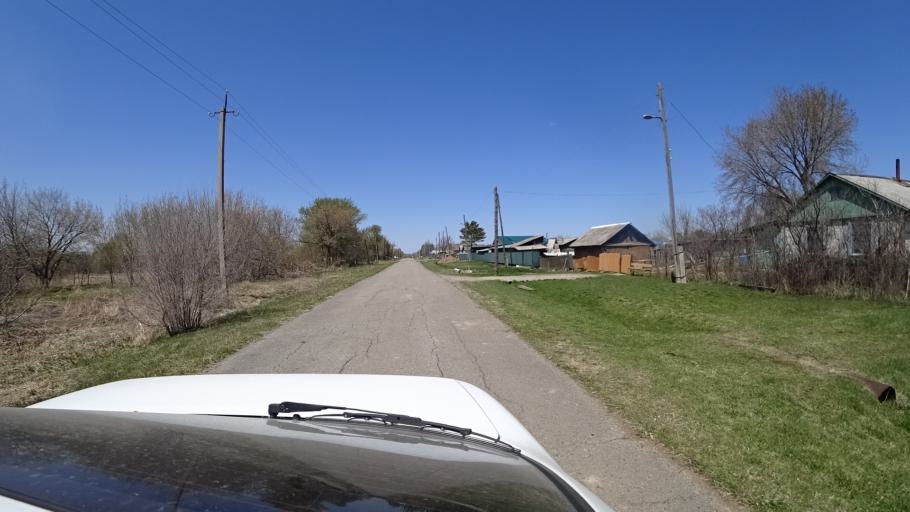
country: RU
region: Primorskiy
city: Lazo
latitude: 45.7906
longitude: 133.7678
